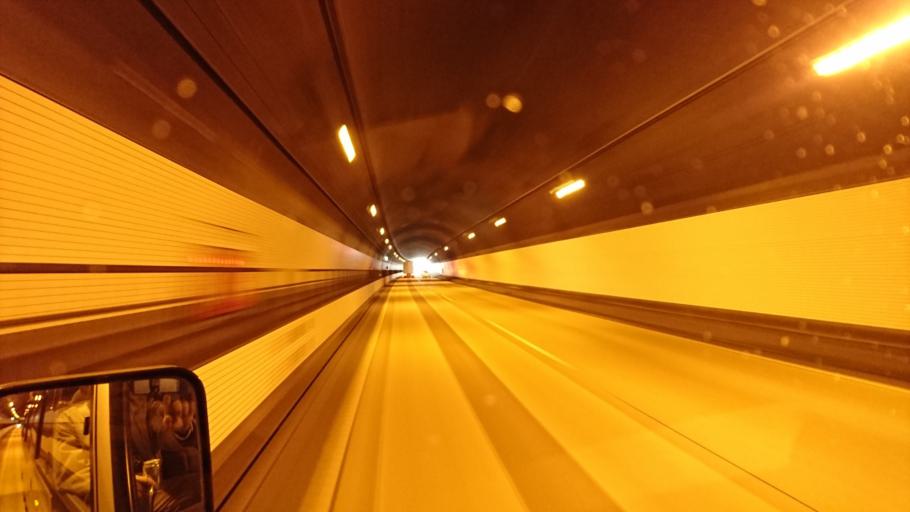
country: JP
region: Hyogo
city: Kakogawacho-honmachi
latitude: 34.8477
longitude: 134.8182
